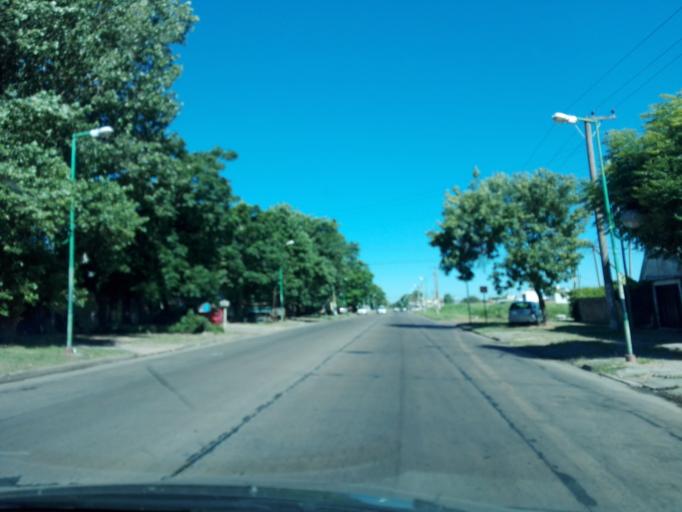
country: AR
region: Buenos Aires
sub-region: Partido de La Plata
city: La Plata
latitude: -34.9239
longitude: -57.9101
